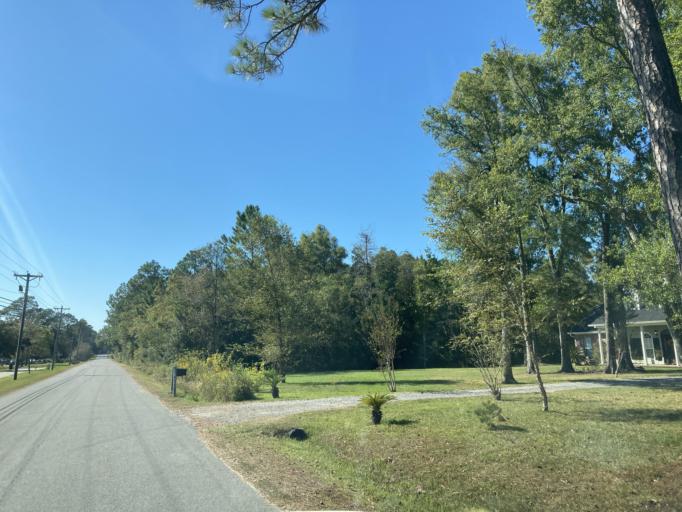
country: US
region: Mississippi
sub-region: Jackson County
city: Saint Martin
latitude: 30.4649
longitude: -88.8507
